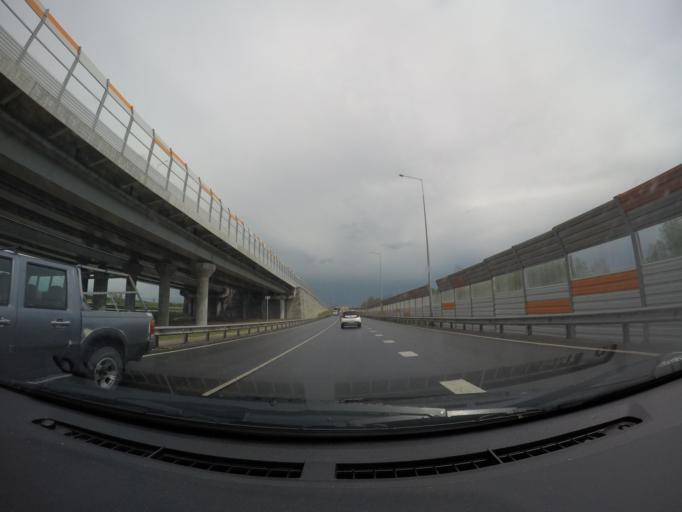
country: RU
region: Moskovskaya
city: Belyye Stolby
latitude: 55.3400
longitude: 37.8230
